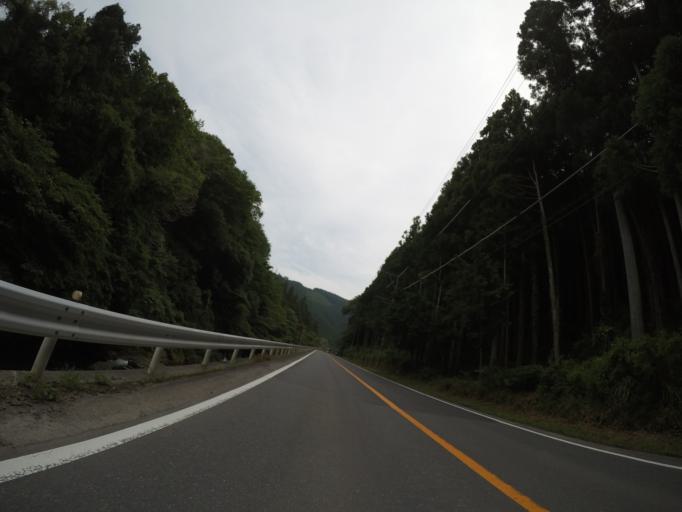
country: JP
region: Shizuoka
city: Fujinomiya
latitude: 35.2002
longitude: 138.5395
